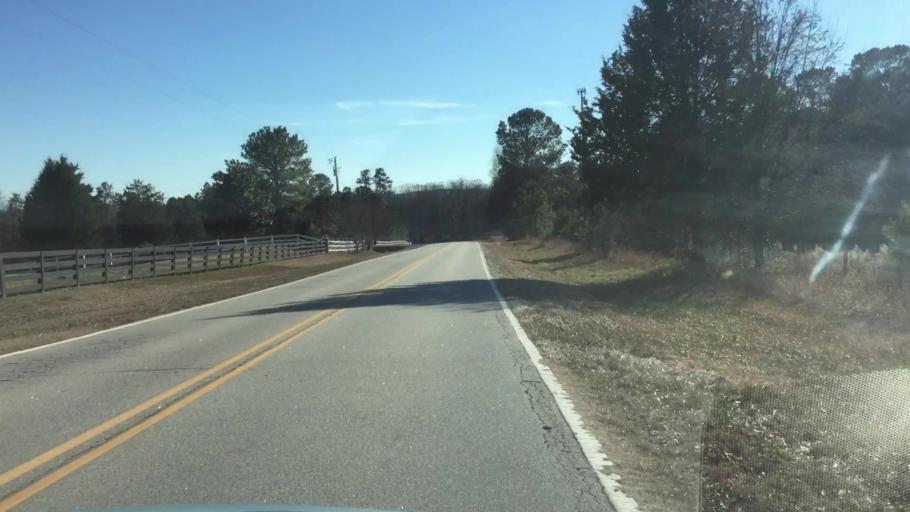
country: US
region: Georgia
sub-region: Newton County
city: Oakwood
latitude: 33.4942
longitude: -84.0471
